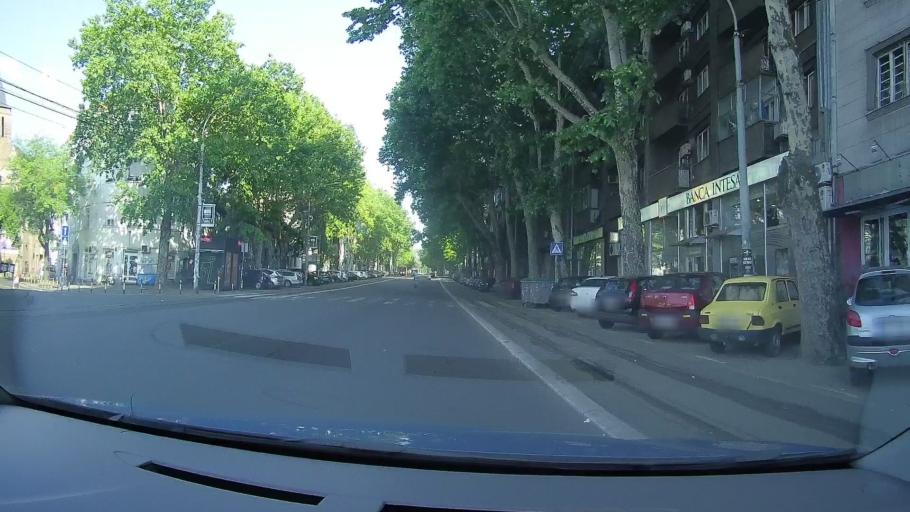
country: RS
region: Central Serbia
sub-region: Belgrade
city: Stari Grad
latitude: 44.8182
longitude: 20.4672
